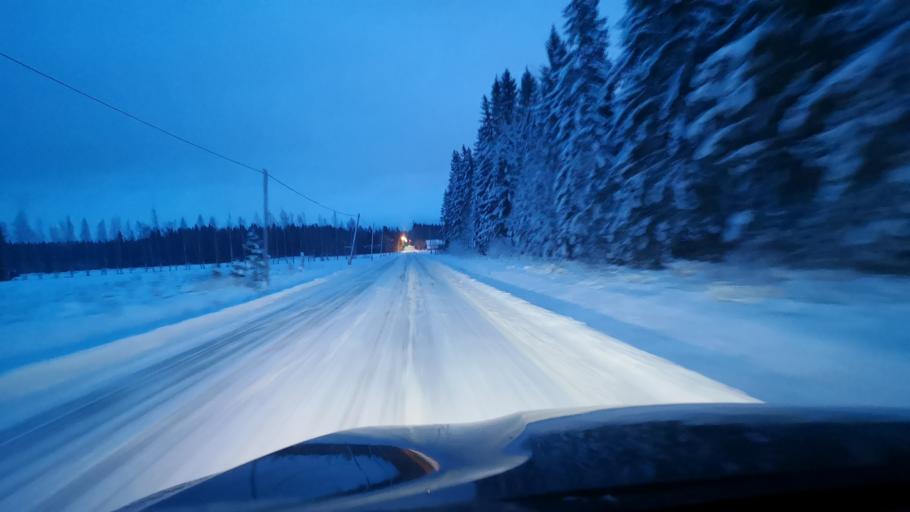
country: FI
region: Varsinais-Suomi
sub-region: Loimaa
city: Loimaa
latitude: 60.8785
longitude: 23.0894
